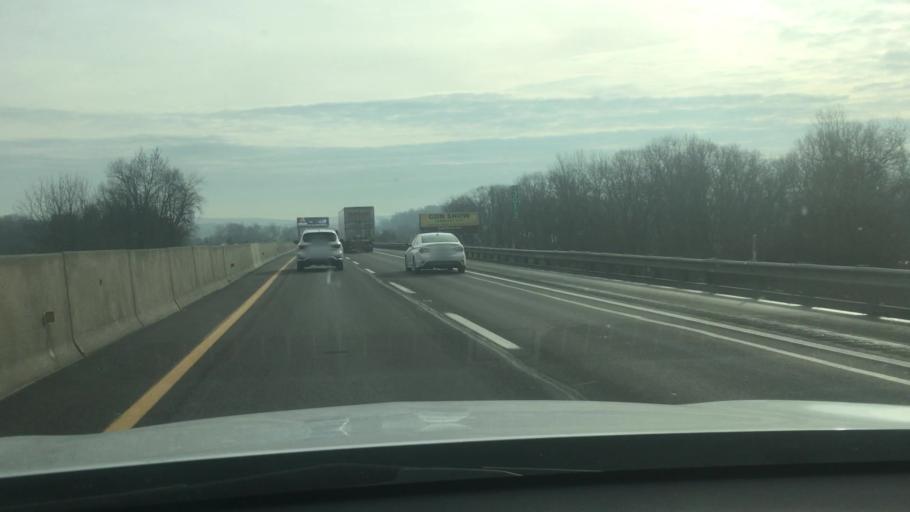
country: US
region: Pennsylvania
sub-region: Chester County
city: Elverson
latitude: 40.1482
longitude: -75.8342
